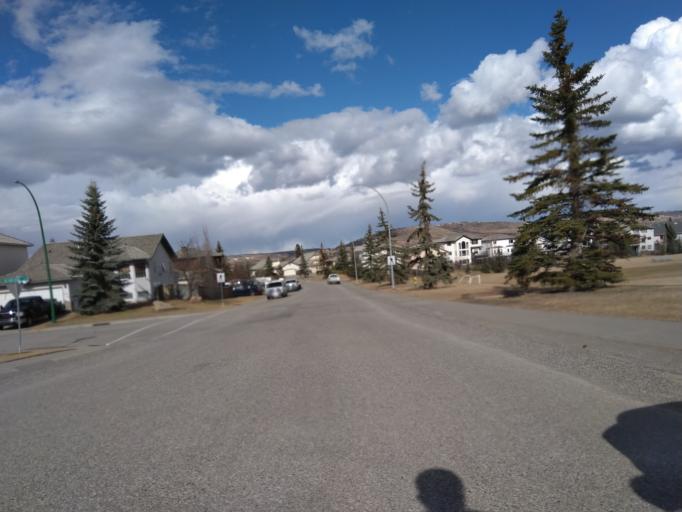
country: CA
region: Alberta
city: Cochrane
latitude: 51.1852
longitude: -114.5073
